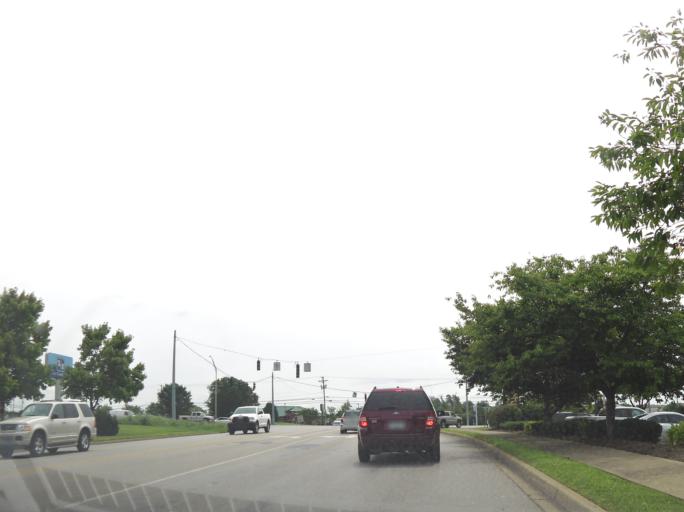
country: US
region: Kentucky
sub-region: Scott County
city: Georgetown
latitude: 38.2312
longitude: -84.5357
